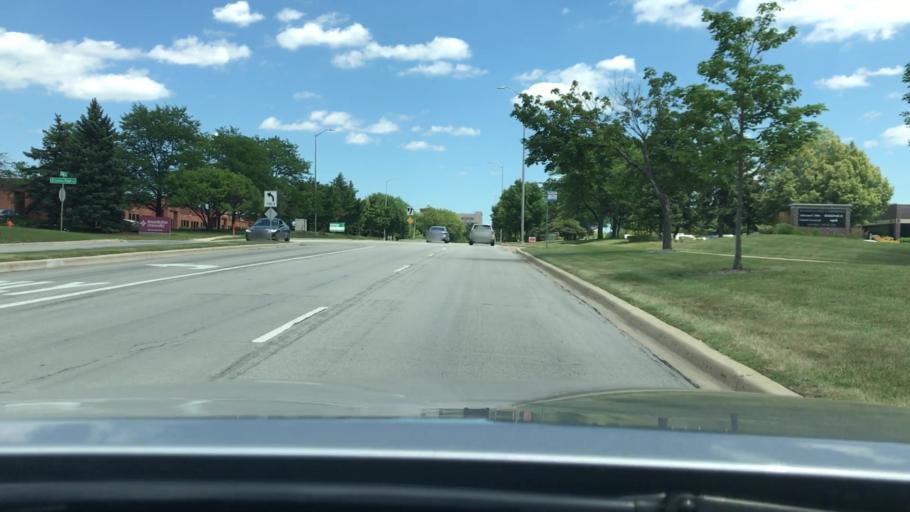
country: US
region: Illinois
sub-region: DuPage County
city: Naperville
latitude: 41.8032
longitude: -88.1363
